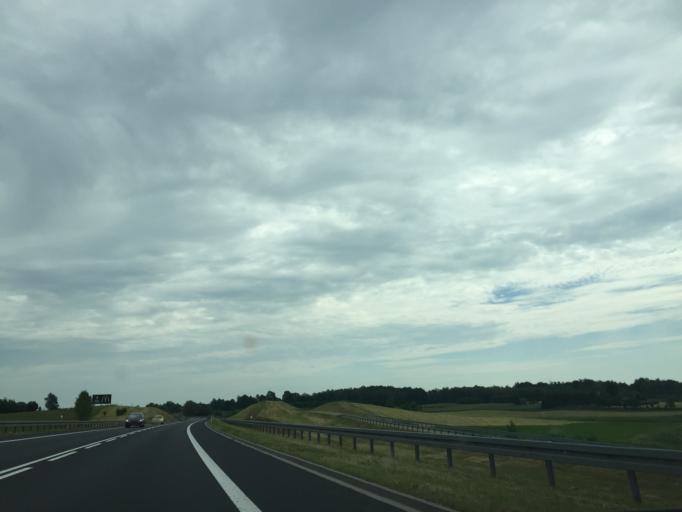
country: PL
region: Warmian-Masurian Voivodeship
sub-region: Powiat olsztynski
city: Biskupiec
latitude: 53.8325
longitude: 20.9088
